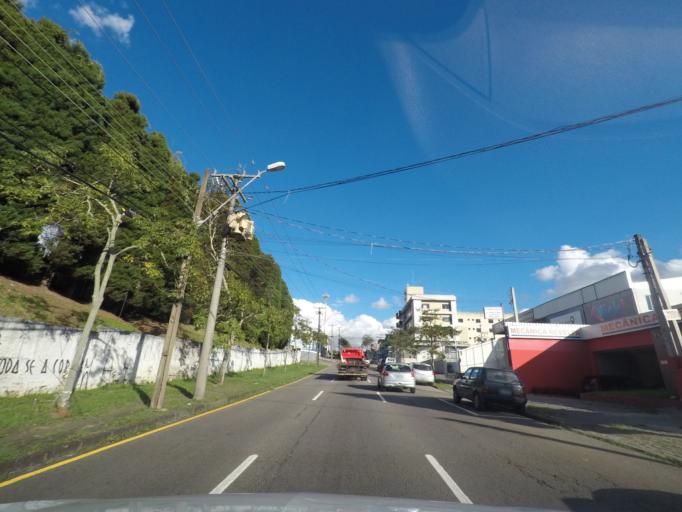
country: BR
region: Parana
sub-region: Curitiba
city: Curitiba
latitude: -25.4586
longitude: -49.2608
